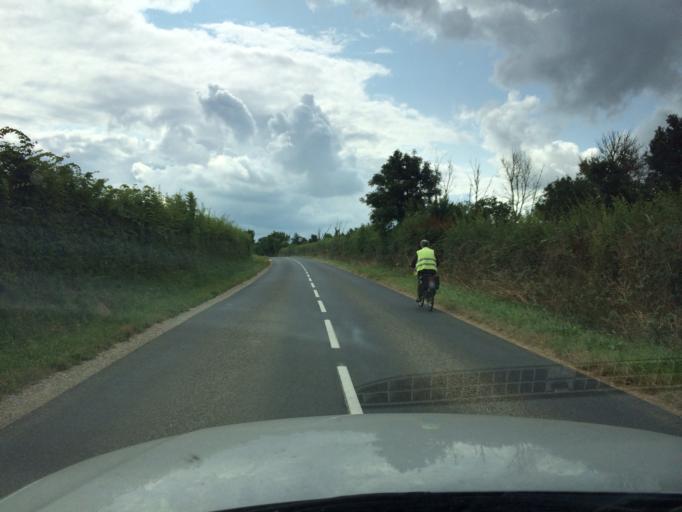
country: FR
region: Lower Normandy
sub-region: Departement de la Manche
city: Sainte-Mere-Eglise
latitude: 49.4508
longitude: -1.2645
